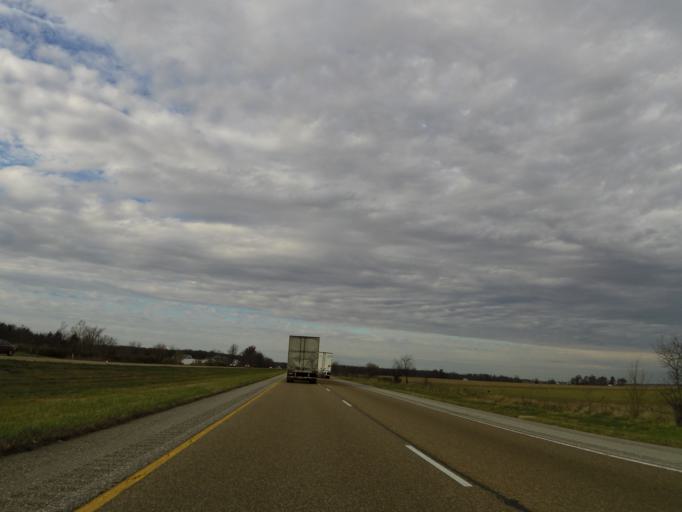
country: US
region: Illinois
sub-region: Washington County
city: Nashville
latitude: 38.3913
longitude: -89.2826
